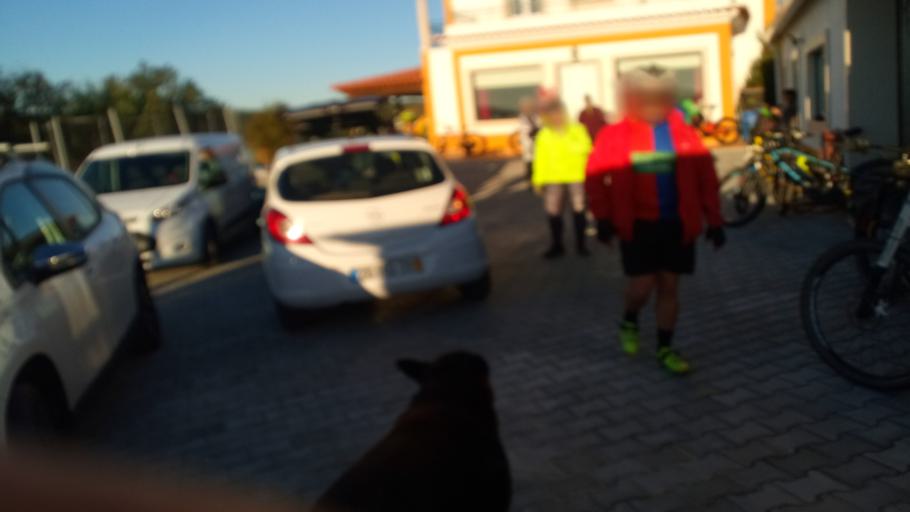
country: PT
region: Leiria
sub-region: Caldas da Rainha
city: Caldas da Rainha
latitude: 39.3819
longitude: -9.0730
